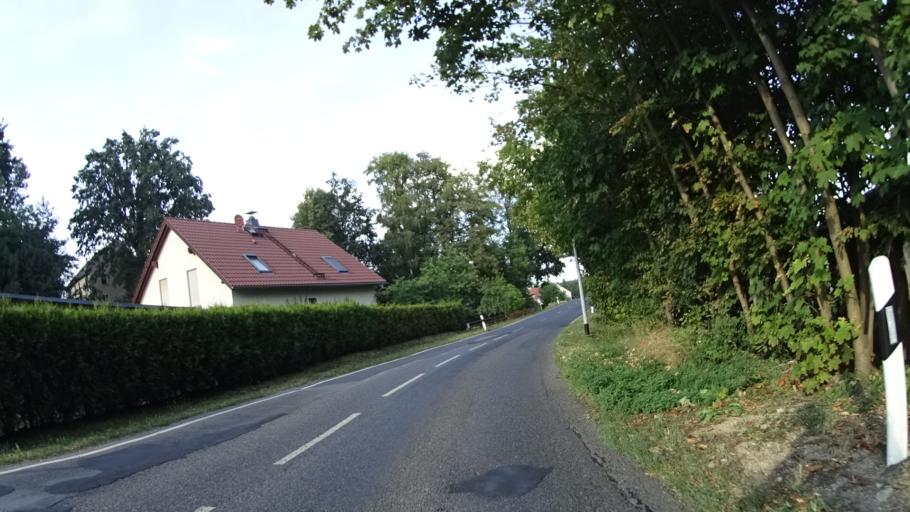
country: DE
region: Saxony
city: Goerlitz
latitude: 51.1812
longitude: 14.9987
